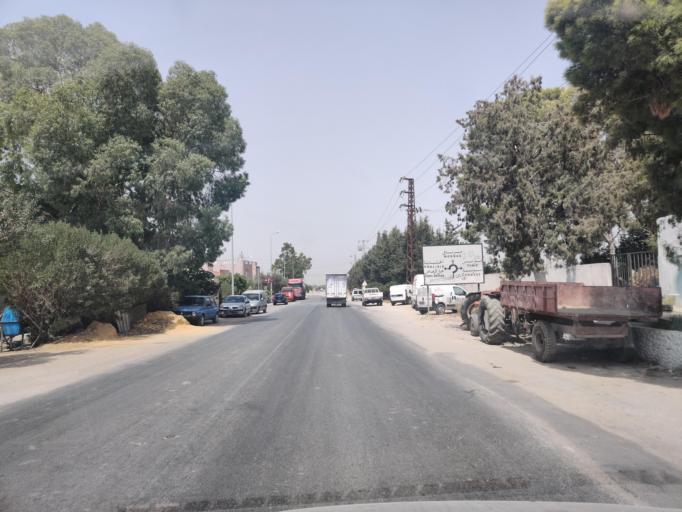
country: TN
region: Tunis
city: La Sebala du Mornag
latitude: 36.6620
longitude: 10.3239
